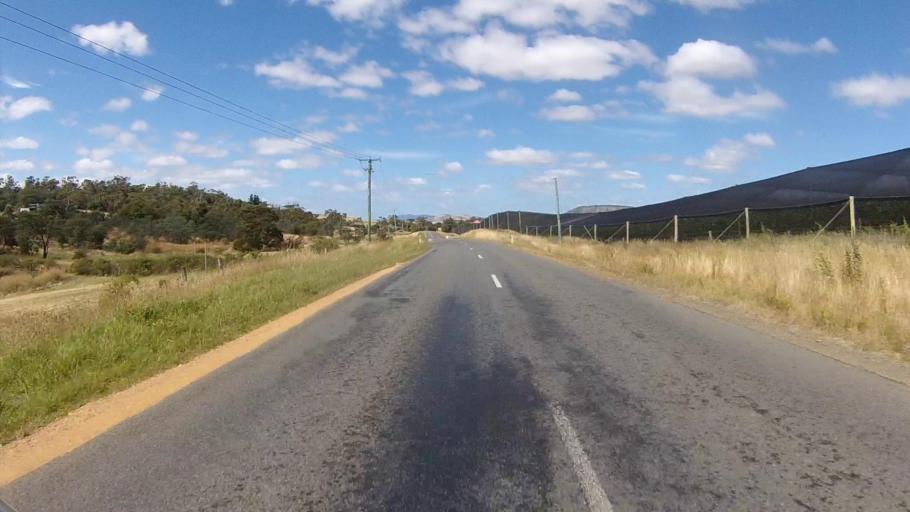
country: AU
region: Tasmania
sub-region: Sorell
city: Sorell
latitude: -42.6460
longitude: 147.4339
